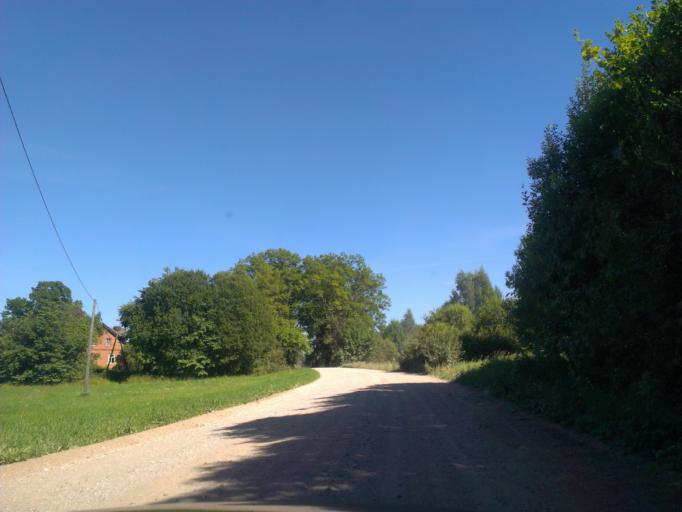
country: LV
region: Malpils
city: Malpils
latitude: 57.0591
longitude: 25.1621
